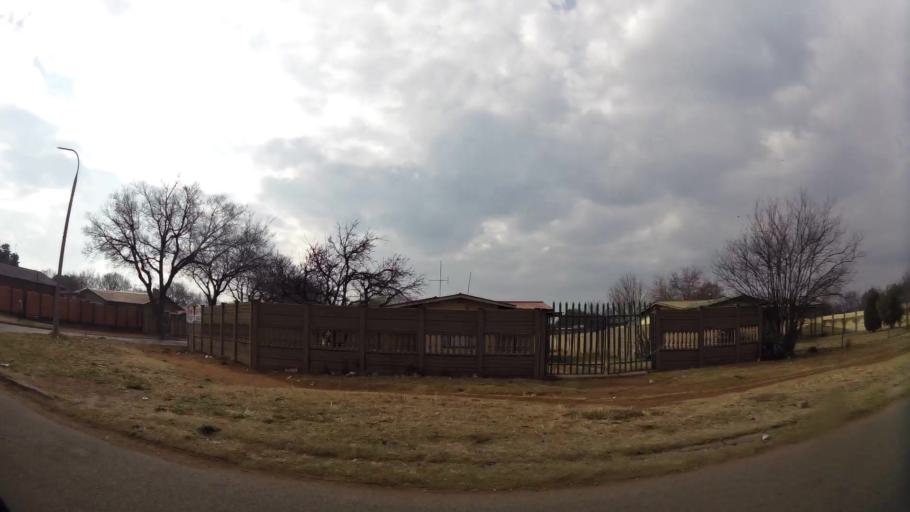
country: ZA
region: Gauteng
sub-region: Sedibeng District Municipality
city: Vanderbijlpark
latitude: -26.6796
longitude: 27.8338
